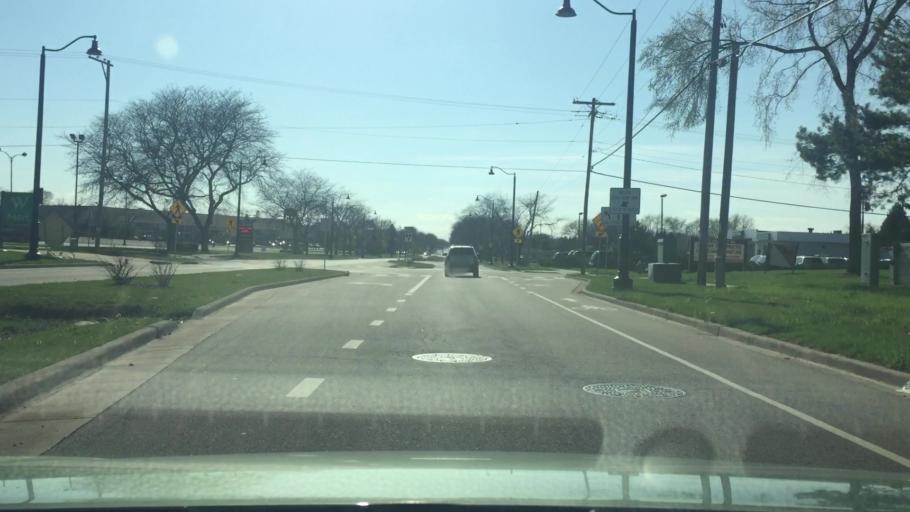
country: US
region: Wisconsin
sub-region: Milwaukee County
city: Brown Deer
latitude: 43.1632
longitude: -87.9691
